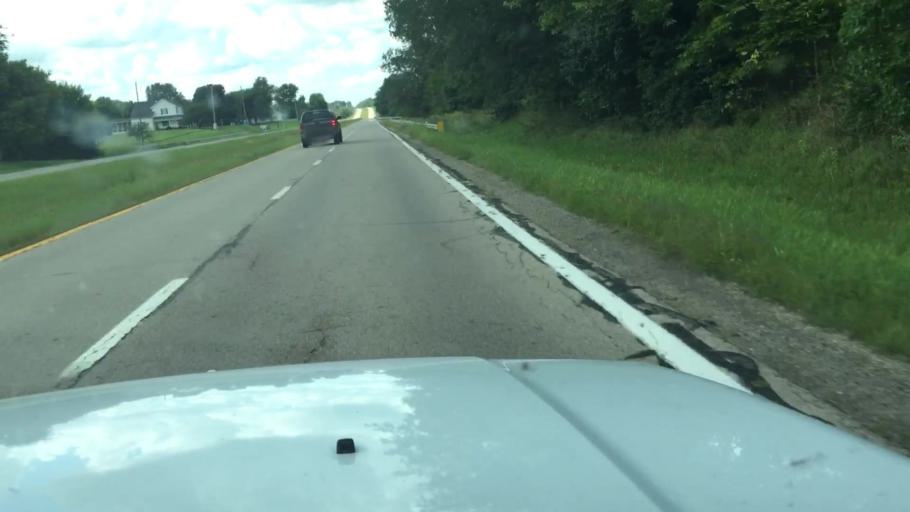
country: US
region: Ohio
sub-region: Madison County
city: Choctaw Lake
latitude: 39.9329
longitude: -83.5120
